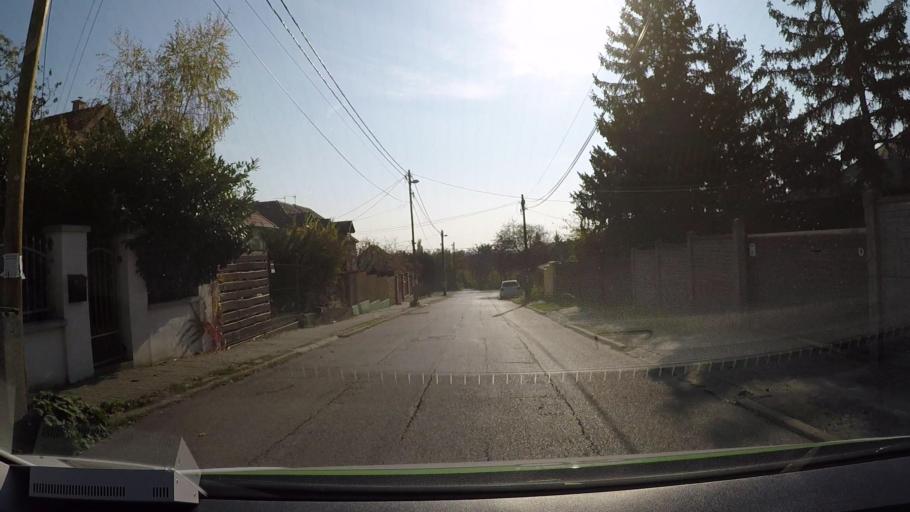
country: HU
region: Budapest
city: Budapest XXII. keruelet
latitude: 47.4165
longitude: 19.0280
